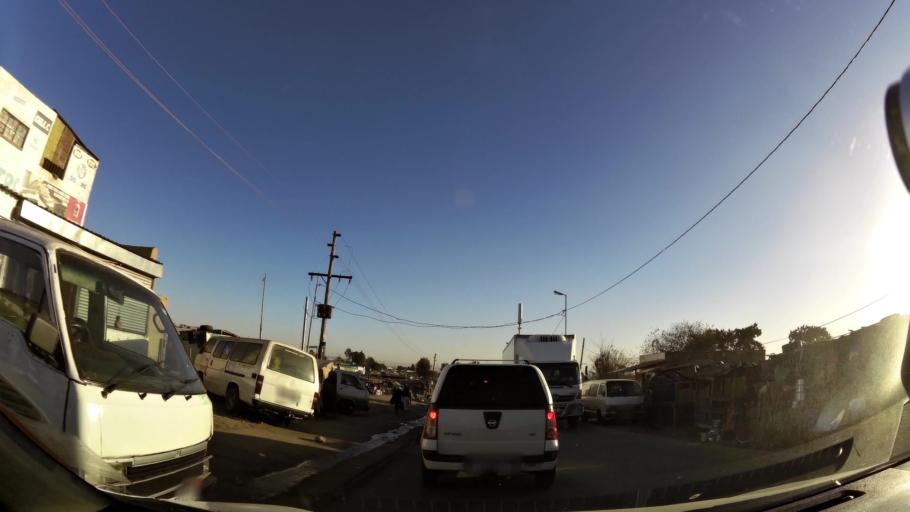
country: ZA
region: Gauteng
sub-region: City of Johannesburg Metropolitan Municipality
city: Diepsloot
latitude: -25.9312
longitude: 28.0162
